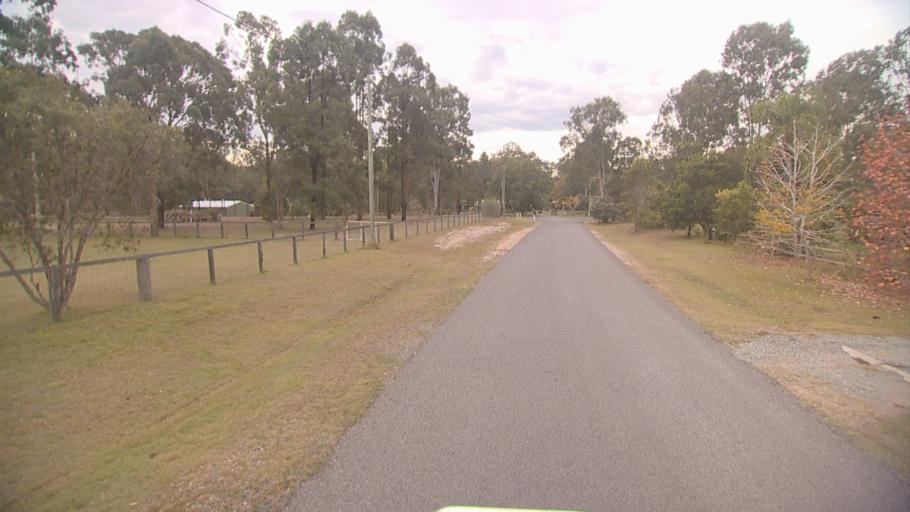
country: AU
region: Queensland
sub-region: Logan
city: Chambers Flat
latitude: -27.8001
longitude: 153.1252
